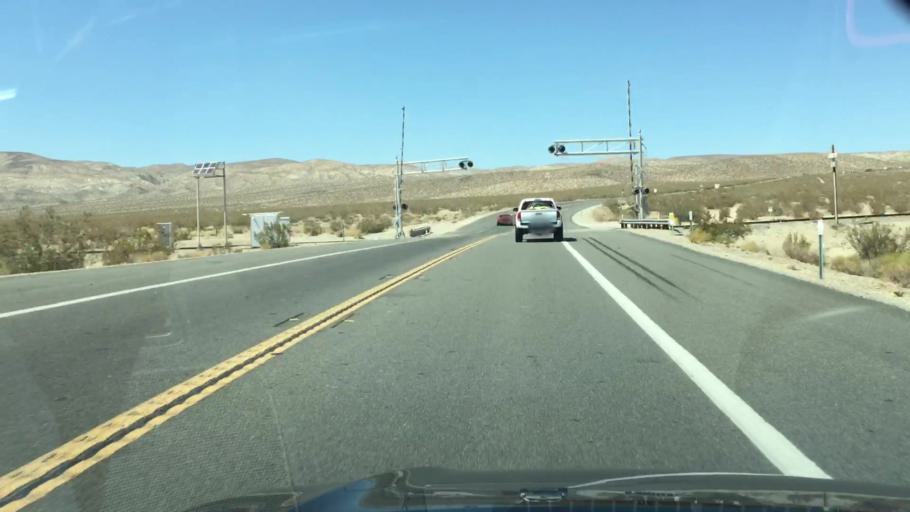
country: US
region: California
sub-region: Kern County
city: Ridgecrest
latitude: 35.4229
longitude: -117.6721
